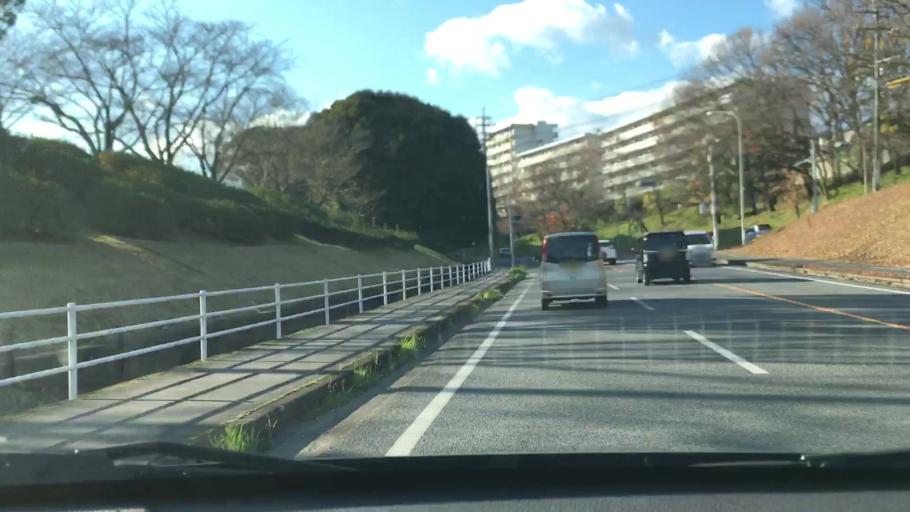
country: JP
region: Oita
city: Oita
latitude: 33.2252
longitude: 131.6512
